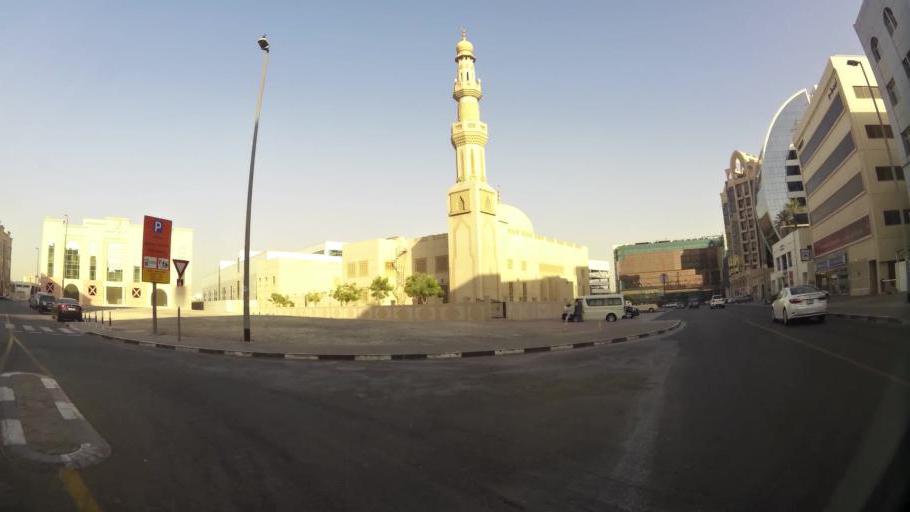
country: AE
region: Ash Shariqah
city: Sharjah
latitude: 25.2452
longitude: 55.3398
